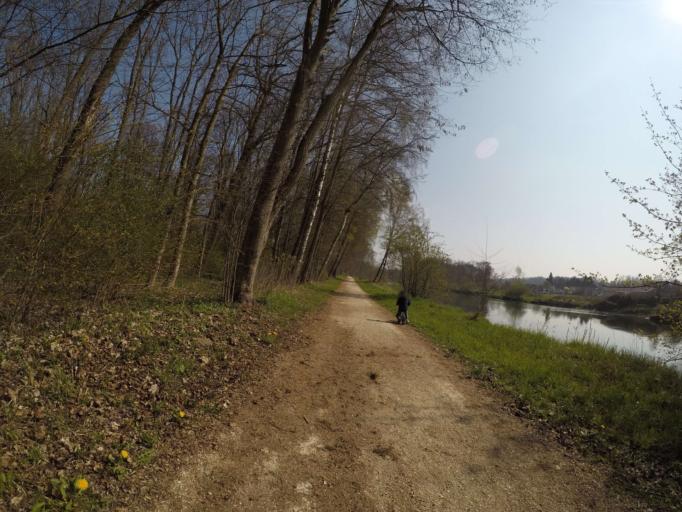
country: DE
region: Bavaria
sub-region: Swabia
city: Guenzburg
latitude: 48.4624
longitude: 10.2740
